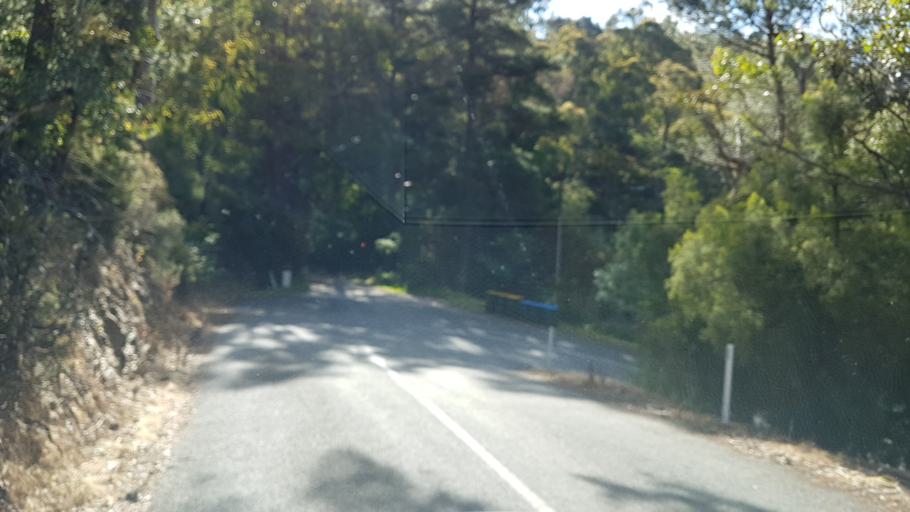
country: AU
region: South Australia
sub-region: Adelaide Hills
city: Adelaide Hills
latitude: -34.9100
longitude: 138.7670
